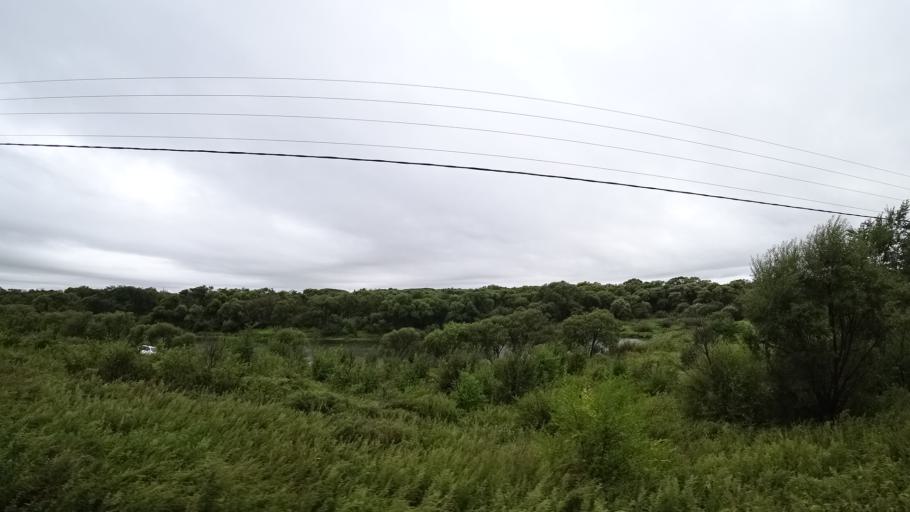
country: RU
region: Primorskiy
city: Monastyrishche
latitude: 44.2675
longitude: 132.4037
